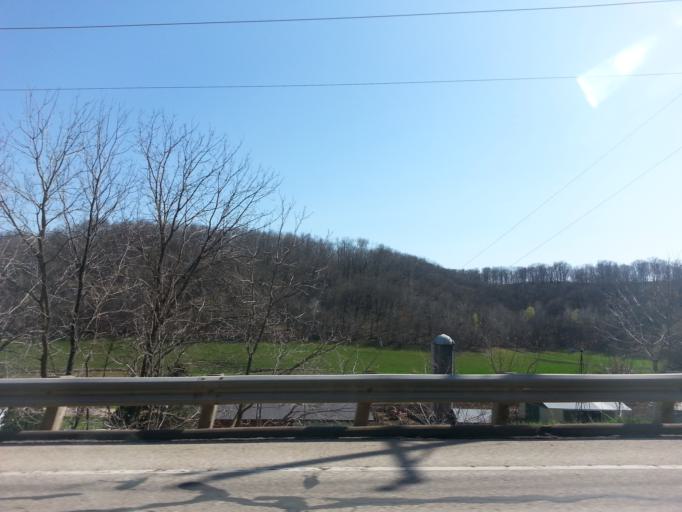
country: US
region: Wisconsin
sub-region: Pepin County
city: Durand
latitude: 44.6408
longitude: -92.1016
